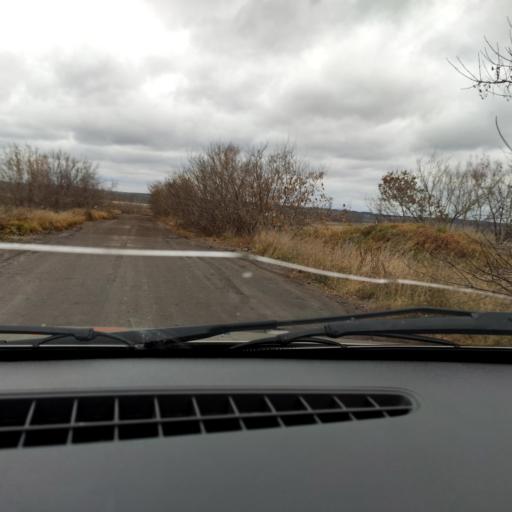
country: RU
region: Bashkortostan
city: Kabakovo
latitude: 54.4762
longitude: 55.9139
